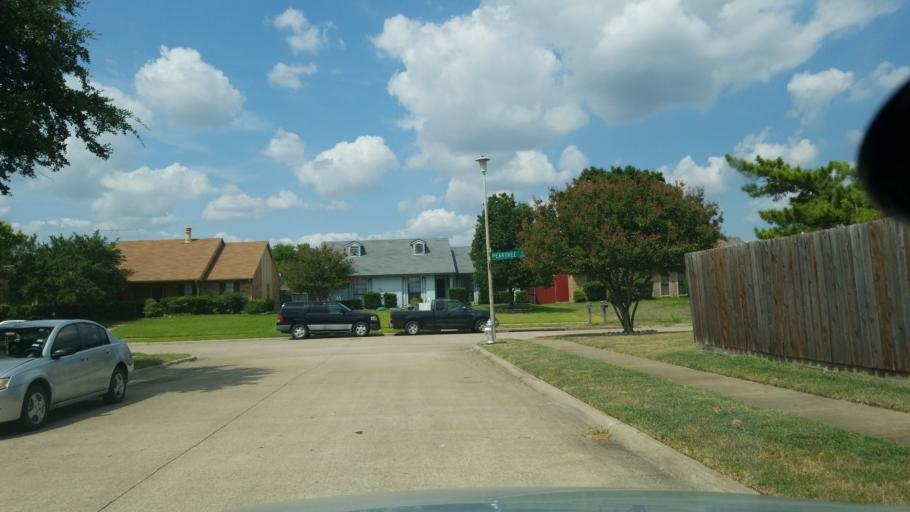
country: US
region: Texas
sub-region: Dallas County
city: Garland
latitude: 32.9214
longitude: -96.6681
